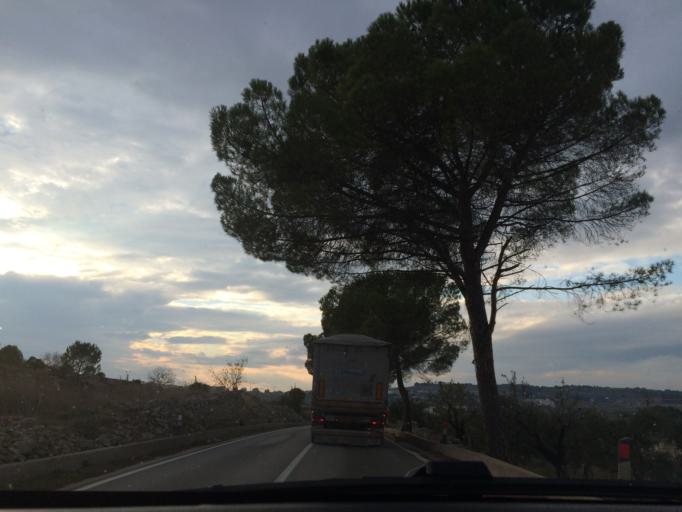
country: IT
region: Basilicate
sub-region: Provincia di Matera
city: Matera
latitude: 40.6804
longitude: 16.6150
